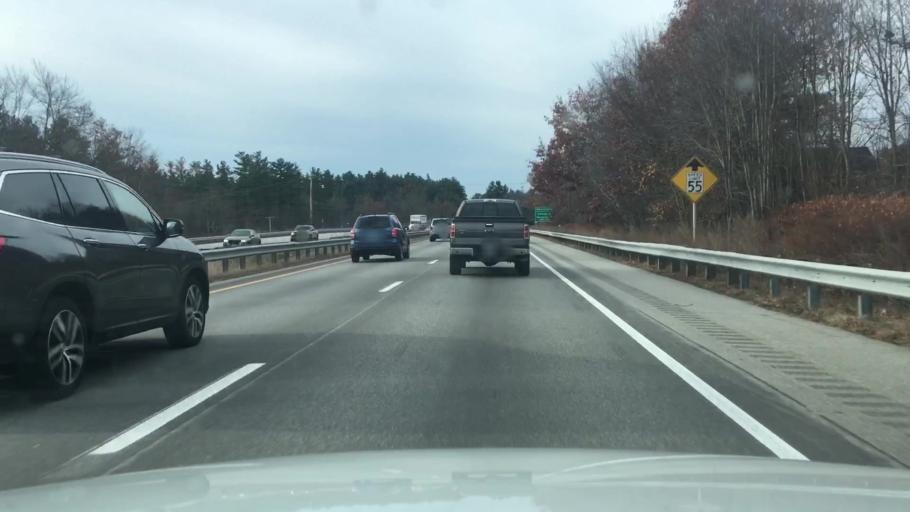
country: US
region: New Hampshire
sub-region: Rockingham County
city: Auburn
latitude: 43.0121
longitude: -71.3825
